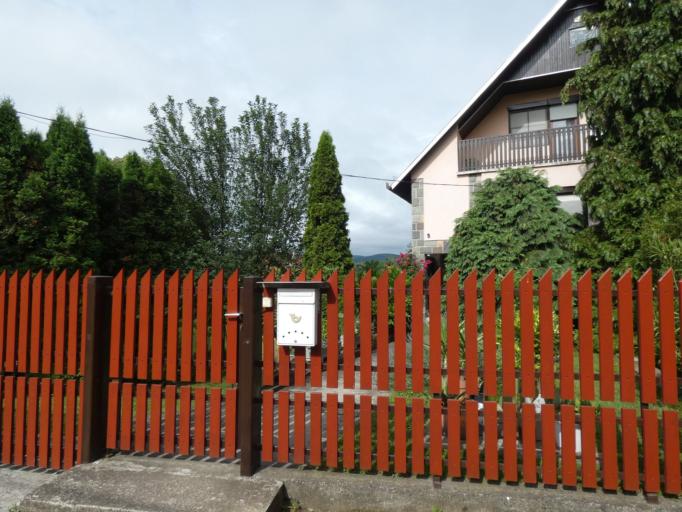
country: HU
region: Pest
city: Kismaros
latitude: 47.8250
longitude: 19.0127
